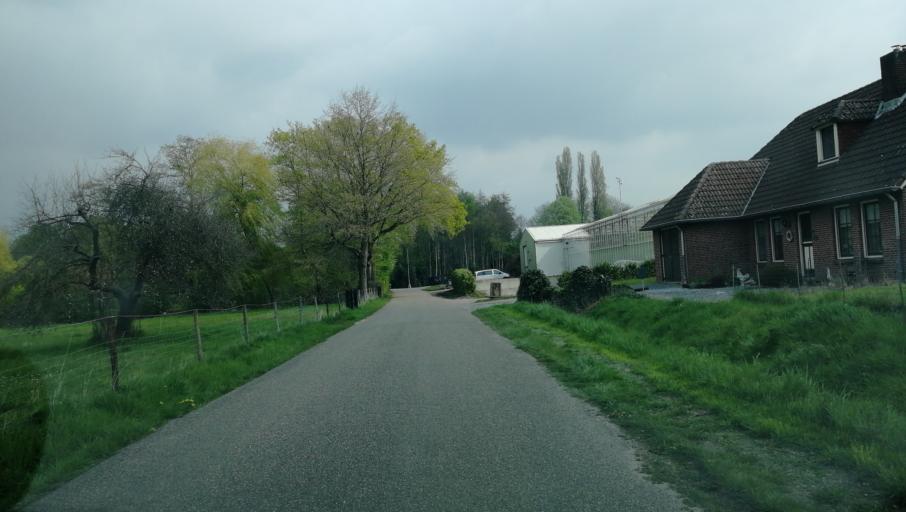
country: NL
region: Limburg
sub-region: Gemeente Venlo
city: Venlo
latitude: 51.3775
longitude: 6.1994
